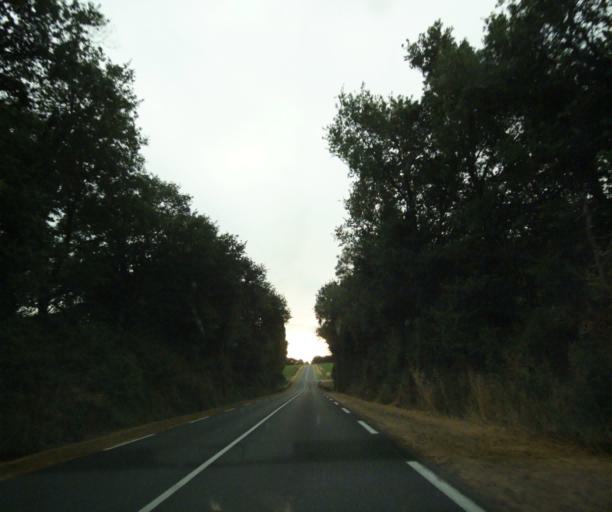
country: FR
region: Pays de la Loire
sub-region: Departement de la Vendee
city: Avrille
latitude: 46.4634
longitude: -1.4611
